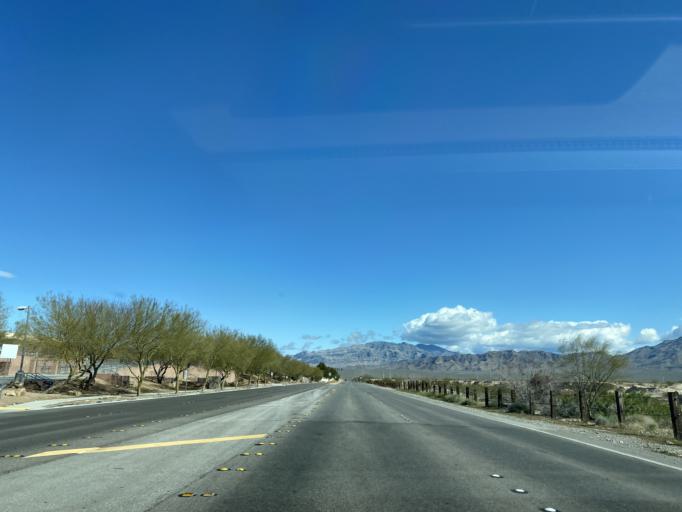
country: US
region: Nevada
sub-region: Clark County
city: North Las Vegas
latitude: 36.3222
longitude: -115.2785
